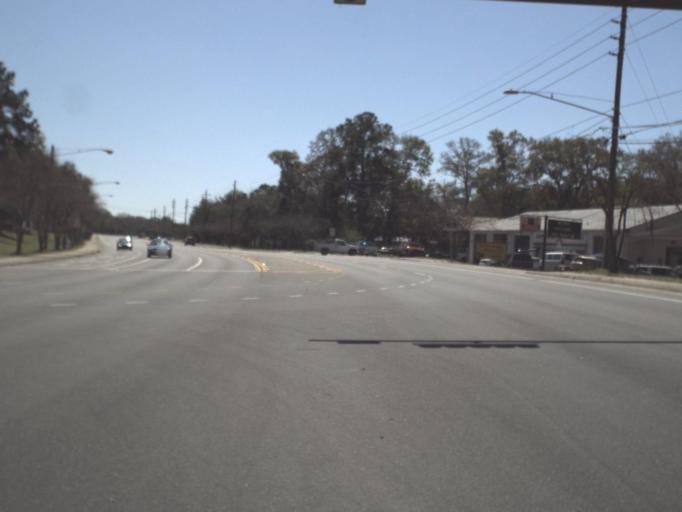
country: US
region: Florida
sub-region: Leon County
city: Tallahassee
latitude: 30.4053
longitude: -84.2837
